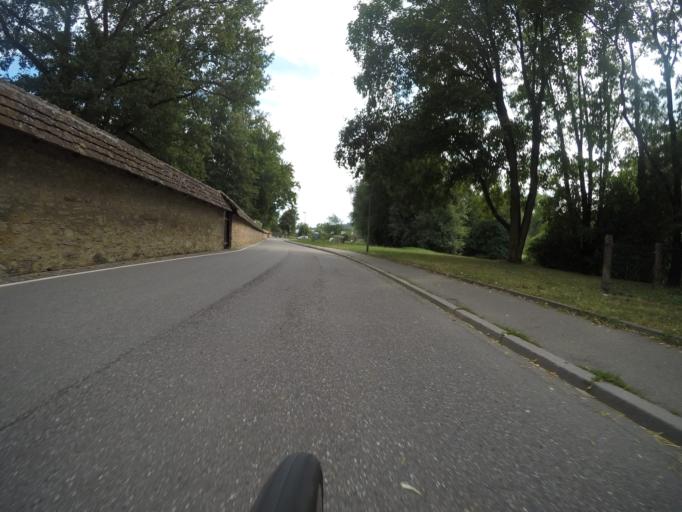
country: DE
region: Baden-Wuerttemberg
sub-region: Regierungsbezirk Stuttgart
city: Weil der Stadt
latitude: 48.7485
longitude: 8.8767
